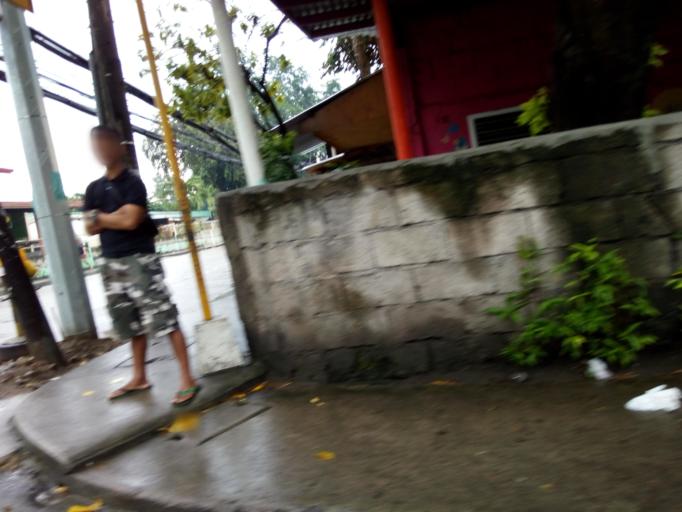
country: PH
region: Central Visayas
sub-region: Province of Negros Oriental
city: Dumaguete
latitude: 9.3082
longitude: 123.3049
